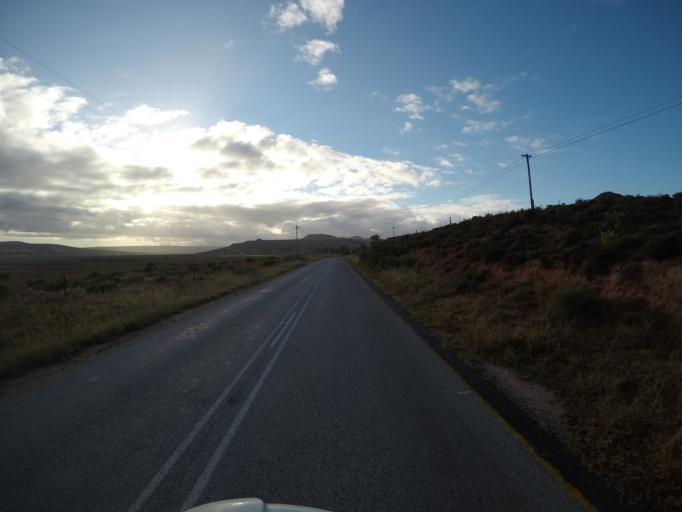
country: ZA
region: Western Cape
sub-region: West Coast District Municipality
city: Clanwilliam
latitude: -32.3250
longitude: 18.3644
